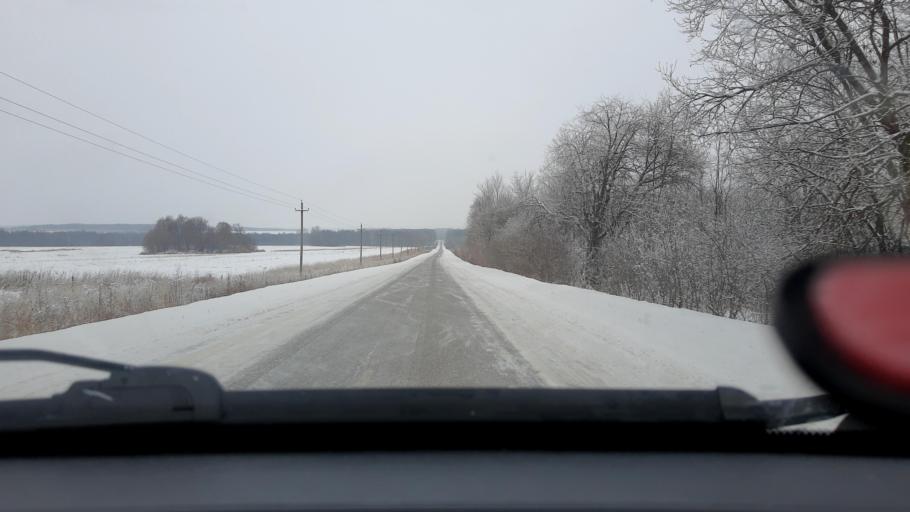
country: RU
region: Bashkortostan
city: Iglino
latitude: 54.6623
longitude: 56.4234
